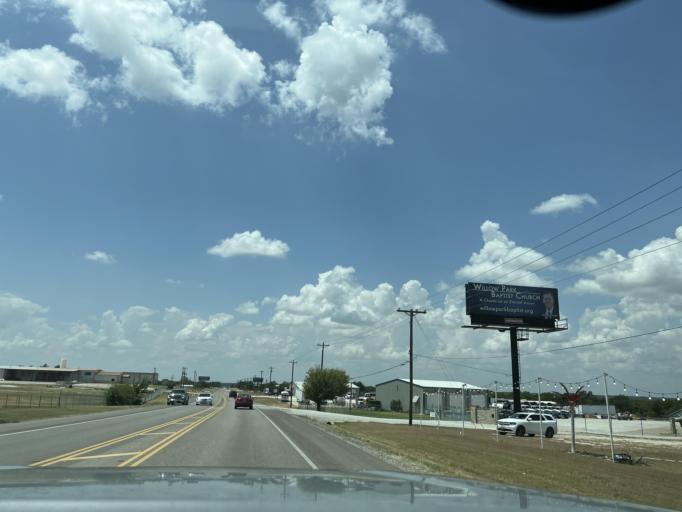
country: US
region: Texas
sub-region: Parker County
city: Weatherford
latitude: 32.8295
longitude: -97.7682
